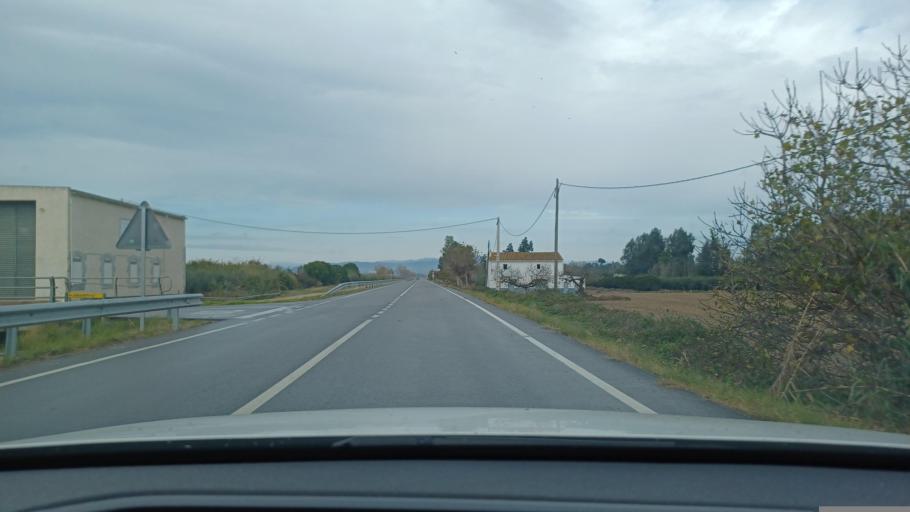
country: ES
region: Catalonia
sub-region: Provincia de Tarragona
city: Amposta
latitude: 40.6711
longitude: 0.5907
